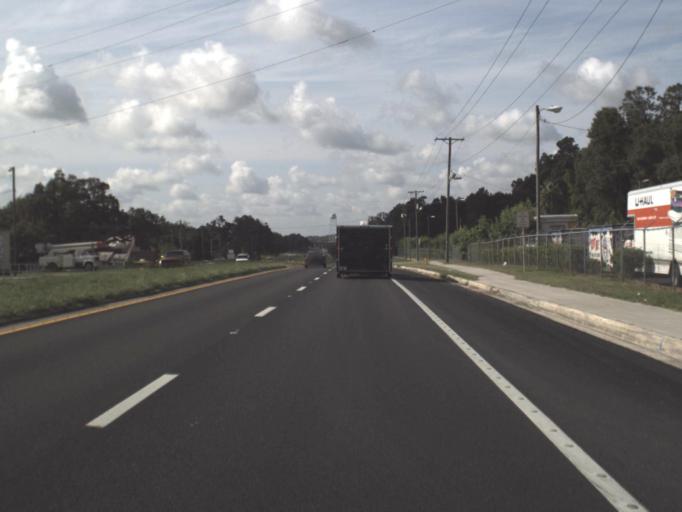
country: US
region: Florida
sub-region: Pasco County
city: Dade City North
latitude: 28.3929
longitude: -82.1952
